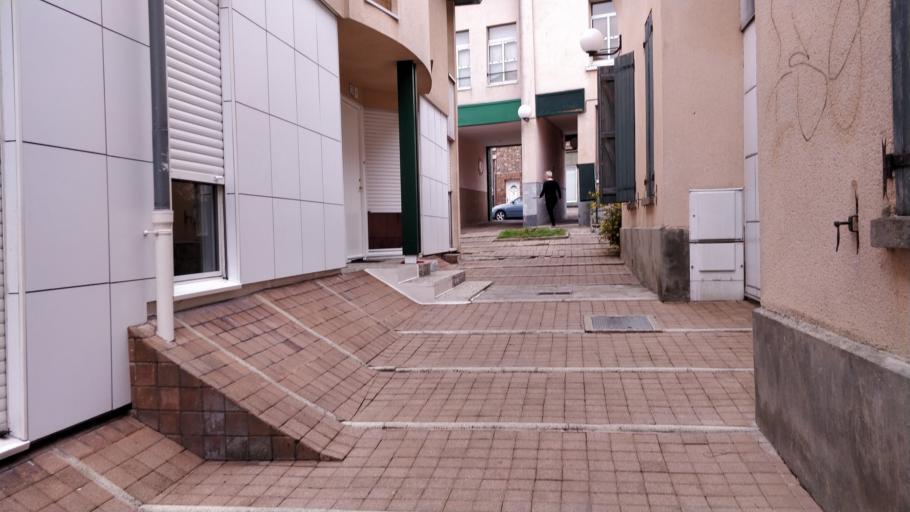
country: FR
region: Picardie
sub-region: Departement de la Somme
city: Amiens
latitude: 49.8862
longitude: 2.2874
